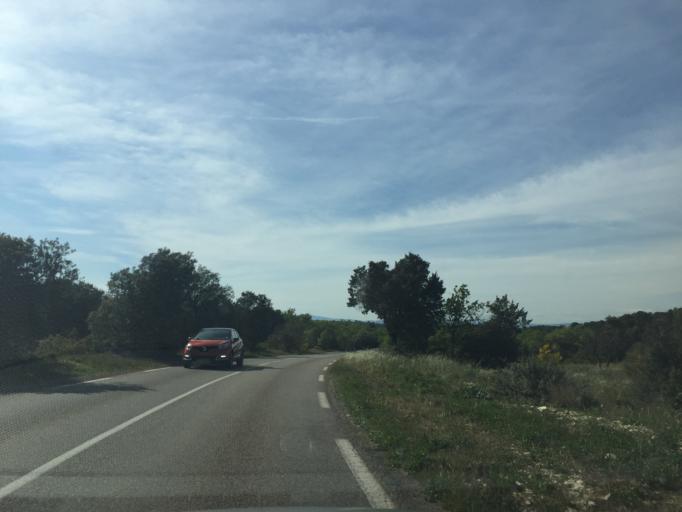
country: FR
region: Provence-Alpes-Cote d'Azur
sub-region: Departement du Var
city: Ginasservis
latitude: 43.6673
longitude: 5.8731
